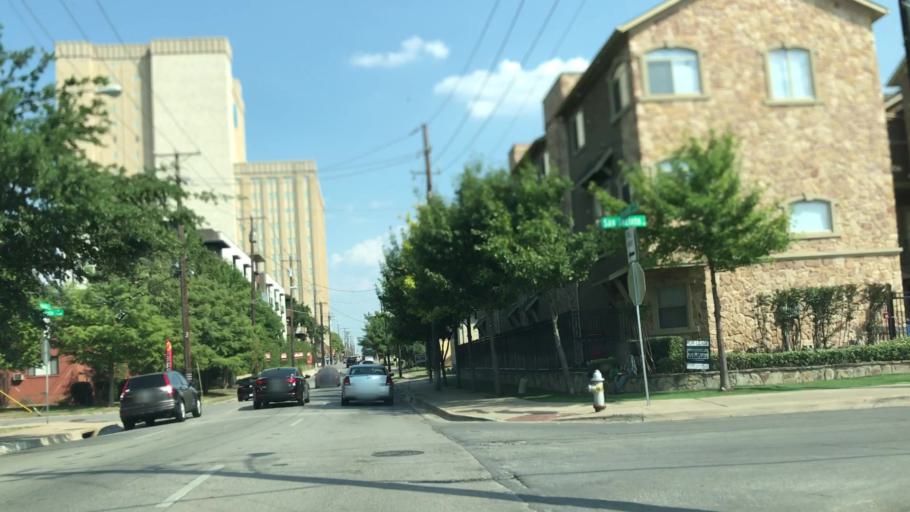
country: US
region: Texas
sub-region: Dallas County
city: Dallas
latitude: 32.7992
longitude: -96.7831
